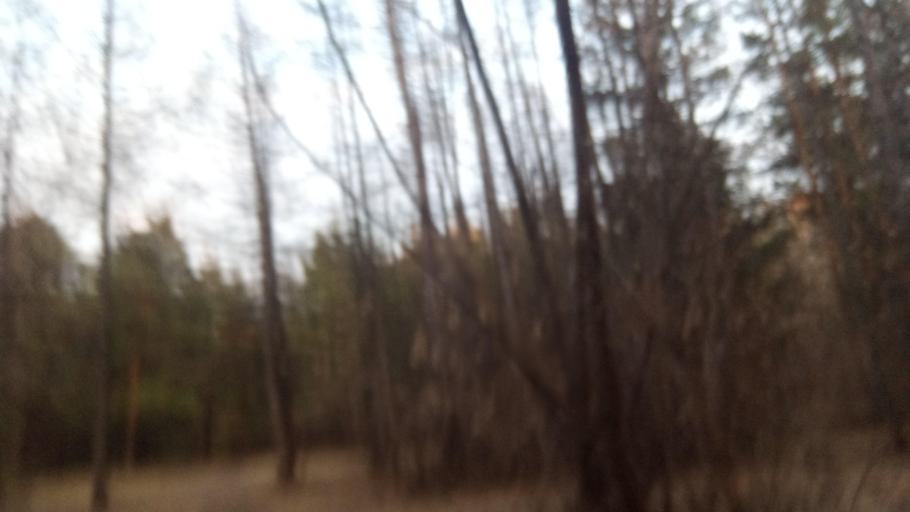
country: RU
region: Chelyabinsk
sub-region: Gorod Chelyabinsk
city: Chelyabinsk
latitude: 55.1567
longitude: 61.3331
